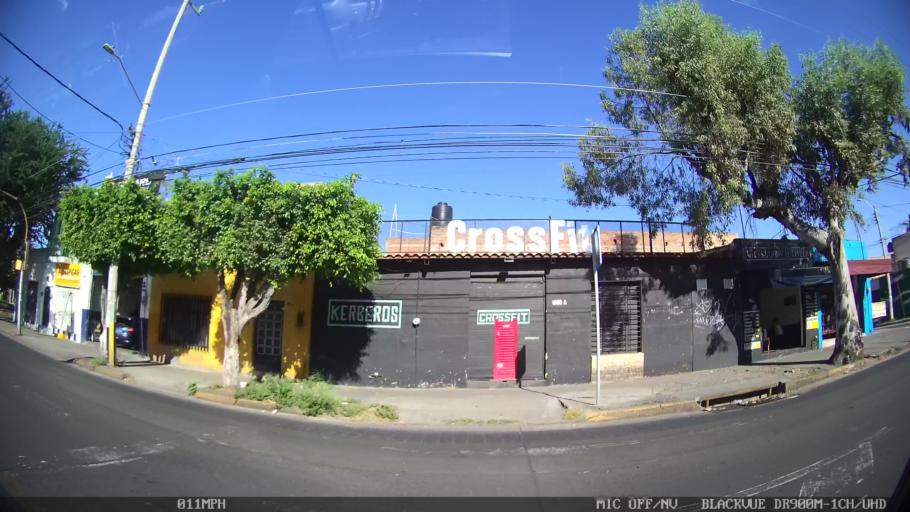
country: MX
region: Jalisco
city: Tlaquepaque
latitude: 20.6988
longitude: -103.3195
